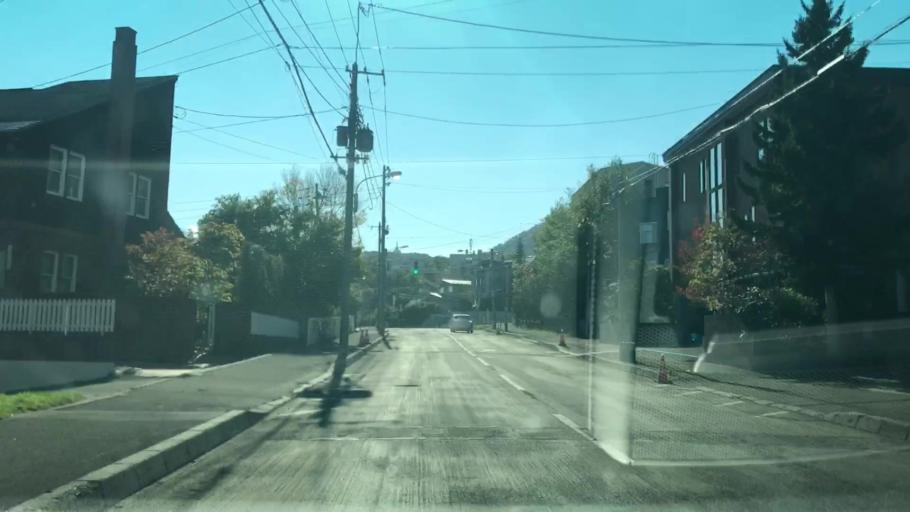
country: JP
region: Hokkaido
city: Sapporo
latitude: 43.0394
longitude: 141.3214
